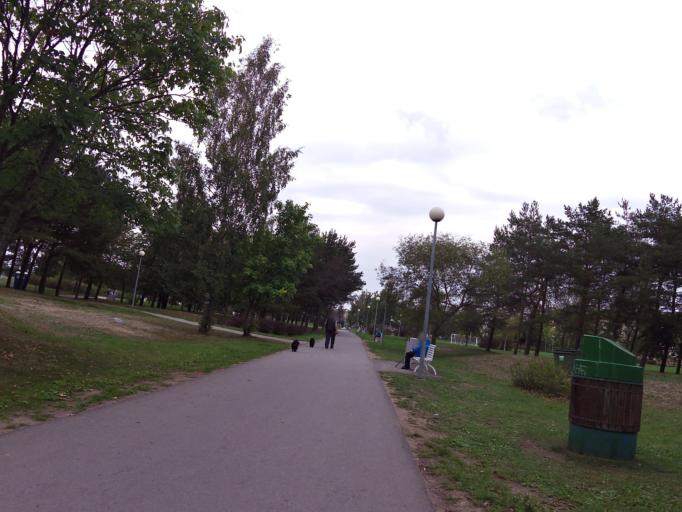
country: EE
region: Harju
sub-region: Tallinna linn
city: Tallinn
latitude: 59.4433
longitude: 24.6856
